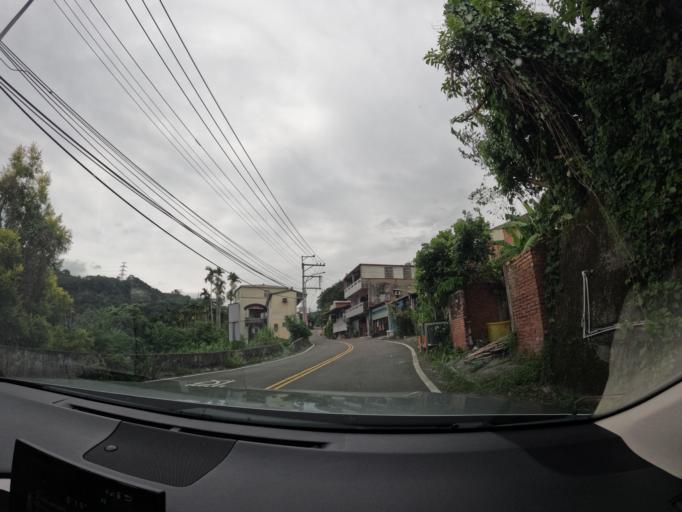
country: TW
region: Taiwan
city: Fengyuan
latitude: 24.3521
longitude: 120.8711
